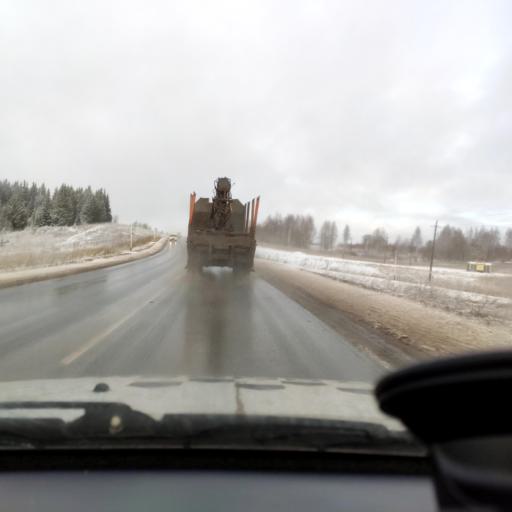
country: RU
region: Perm
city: Nytva
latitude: 57.9551
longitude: 55.3575
